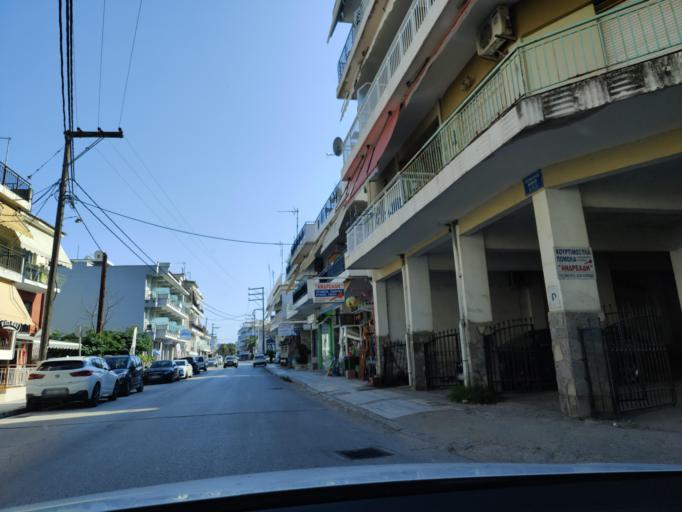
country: GR
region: East Macedonia and Thrace
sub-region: Nomos Kavalas
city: Nea Peramos
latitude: 40.8437
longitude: 24.3060
